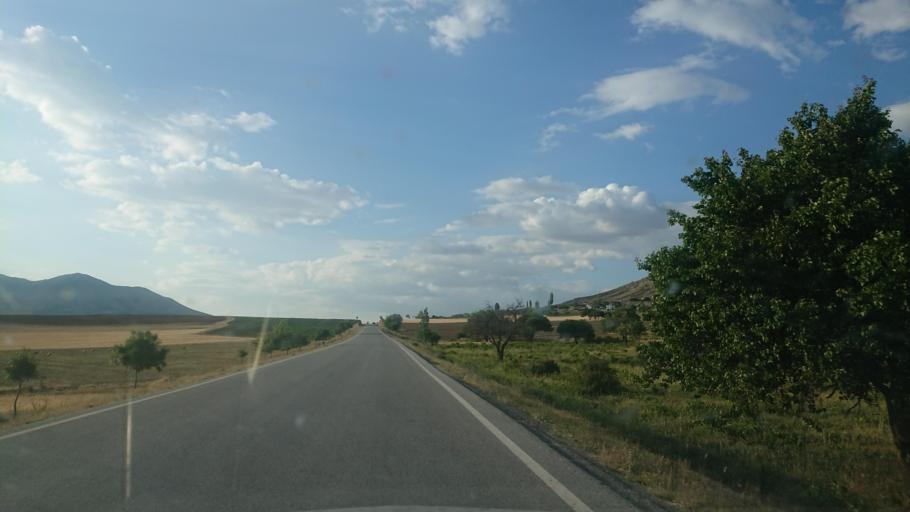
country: TR
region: Aksaray
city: Balci
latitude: 38.5866
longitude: 34.1024
